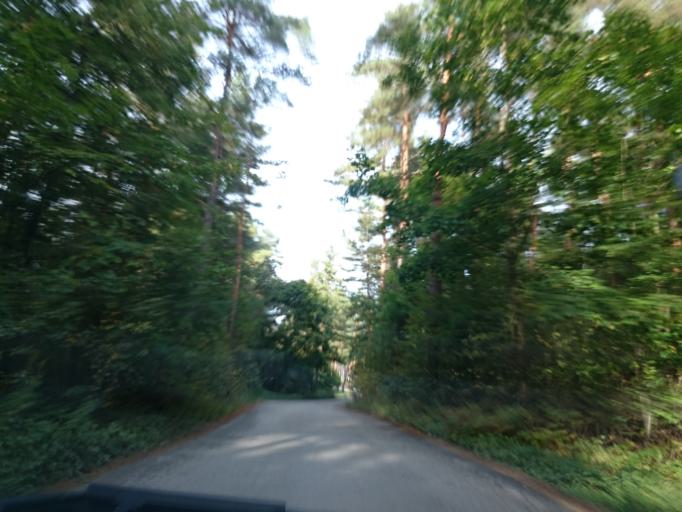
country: LV
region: Adazi
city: Adazi
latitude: 57.0383
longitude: 24.3310
